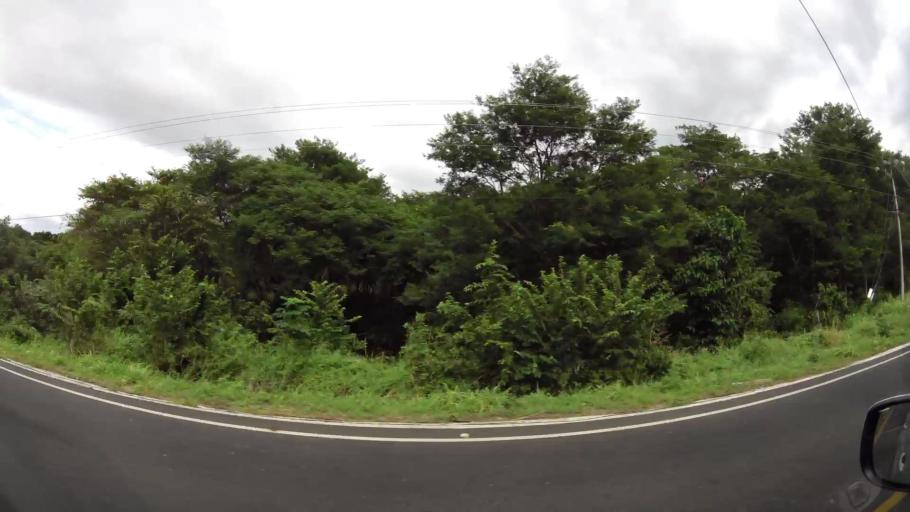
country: CR
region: Guanacaste
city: Nandayure
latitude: 10.2444
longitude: -85.2234
